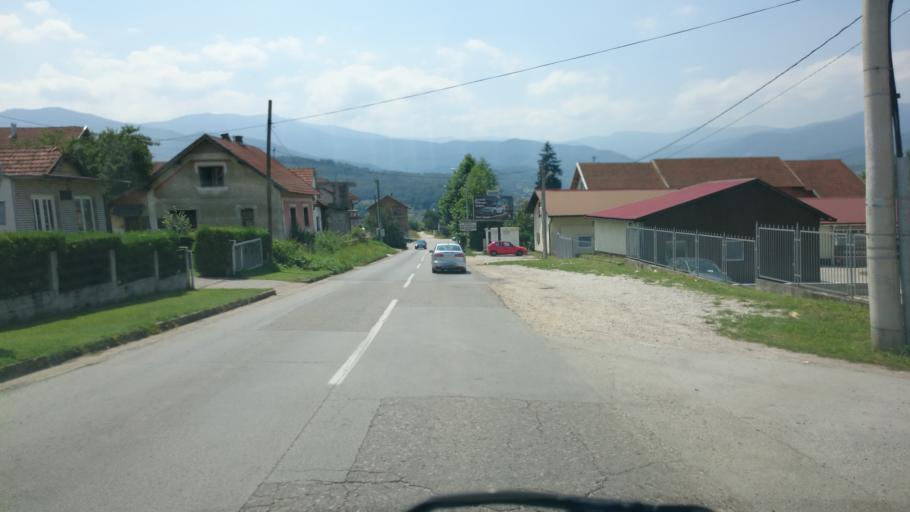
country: BA
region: Federation of Bosnia and Herzegovina
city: Vitez
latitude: 44.1520
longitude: 17.8129
